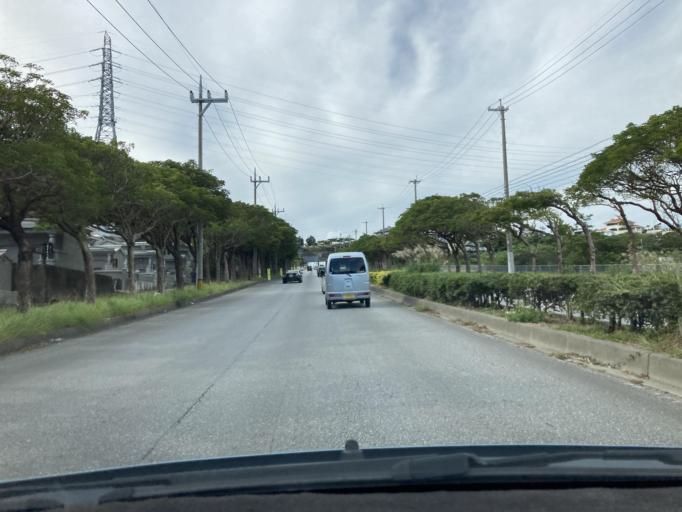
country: JP
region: Okinawa
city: Gushikawa
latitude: 26.3438
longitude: 127.8402
